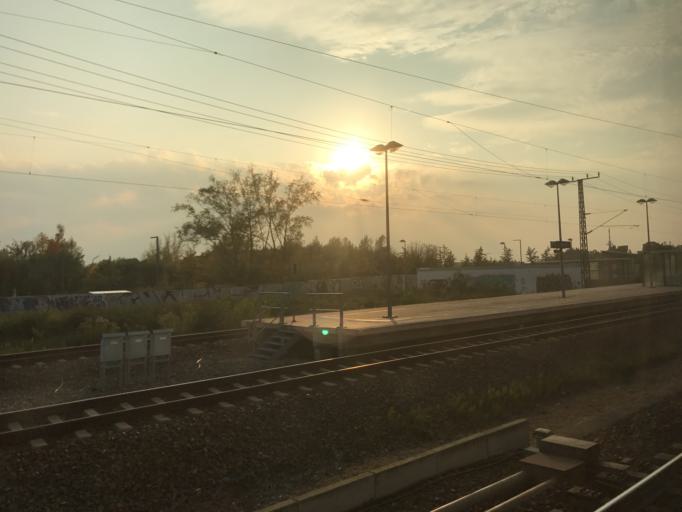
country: DE
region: Saxony
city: Leipzig
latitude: 51.3799
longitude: 12.3234
